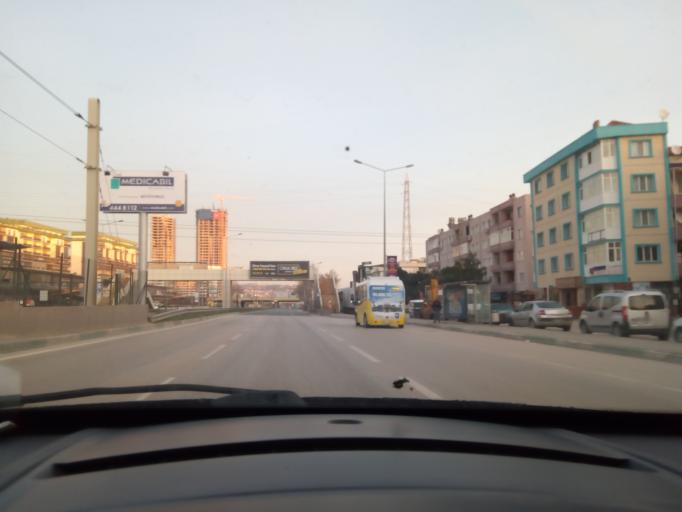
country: TR
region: Bursa
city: Niluefer
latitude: 40.2605
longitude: 28.9513
